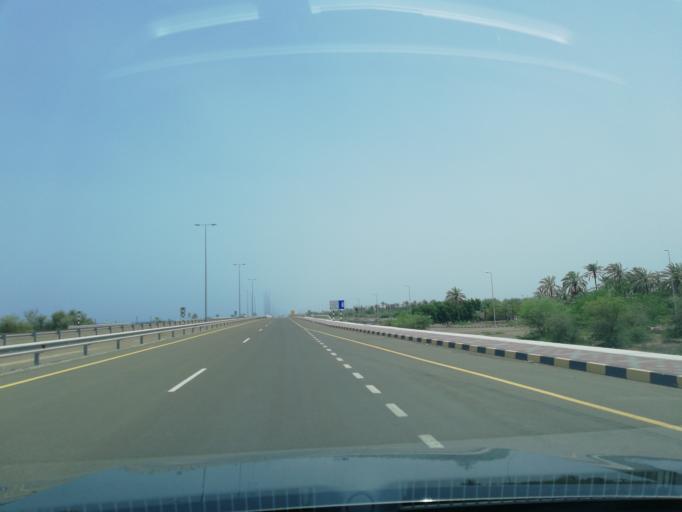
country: OM
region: Al Batinah
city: Al Liwa'
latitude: 24.6400
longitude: 56.5210
